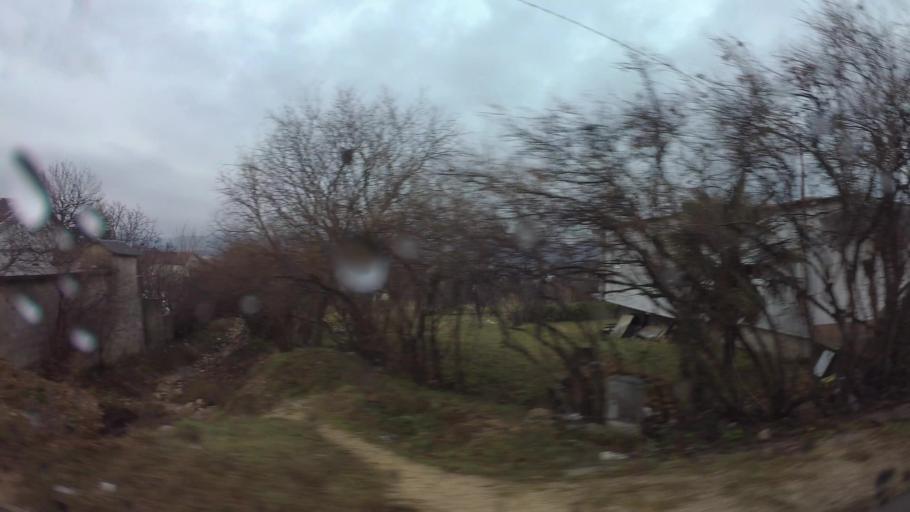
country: BA
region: Federation of Bosnia and Herzegovina
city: Blagaj
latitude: 43.2915
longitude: 17.8589
